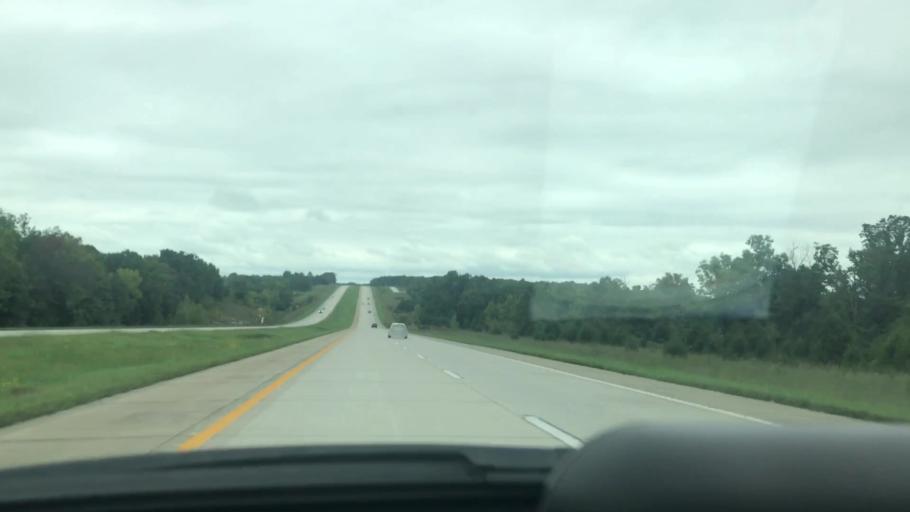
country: US
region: Missouri
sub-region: Dallas County
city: Buffalo
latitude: 37.5443
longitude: -93.1377
